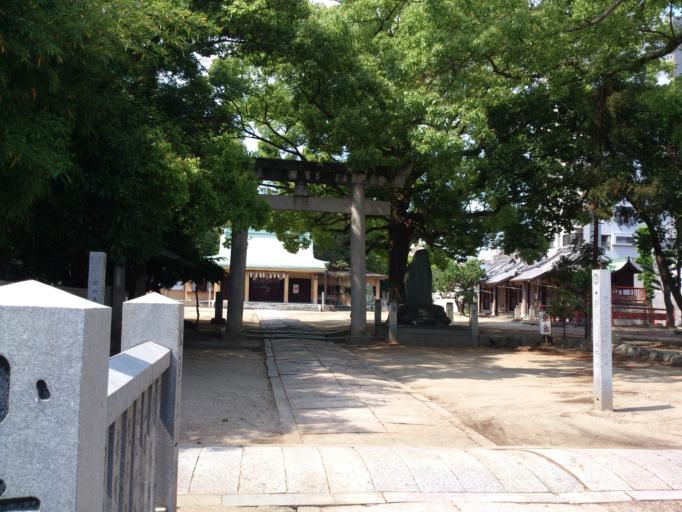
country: JP
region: Ehime
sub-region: Shikoku-chuo Shi
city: Matsuyama
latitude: 33.8455
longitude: 132.7564
